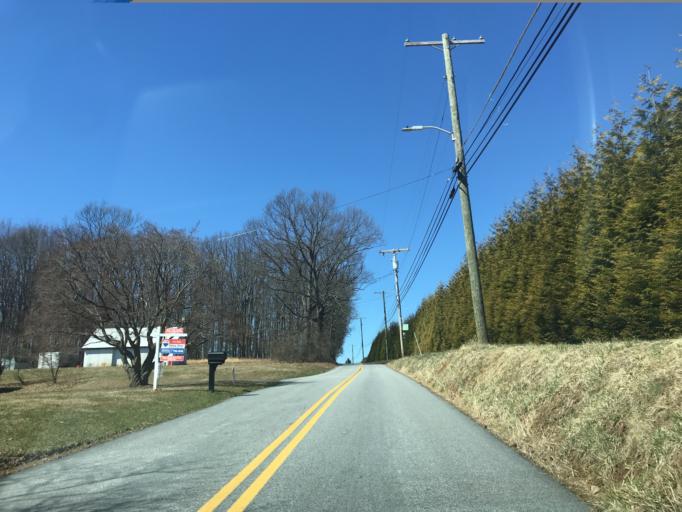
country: US
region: Pennsylvania
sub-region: York County
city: New Freedom
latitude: 39.6835
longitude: -76.6841
